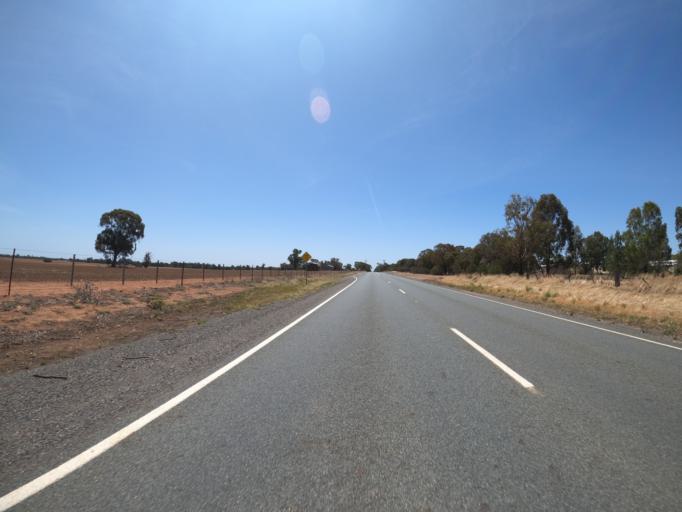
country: AU
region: Victoria
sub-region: Moira
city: Yarrawonga
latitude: -36.0500
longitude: 145.9955
